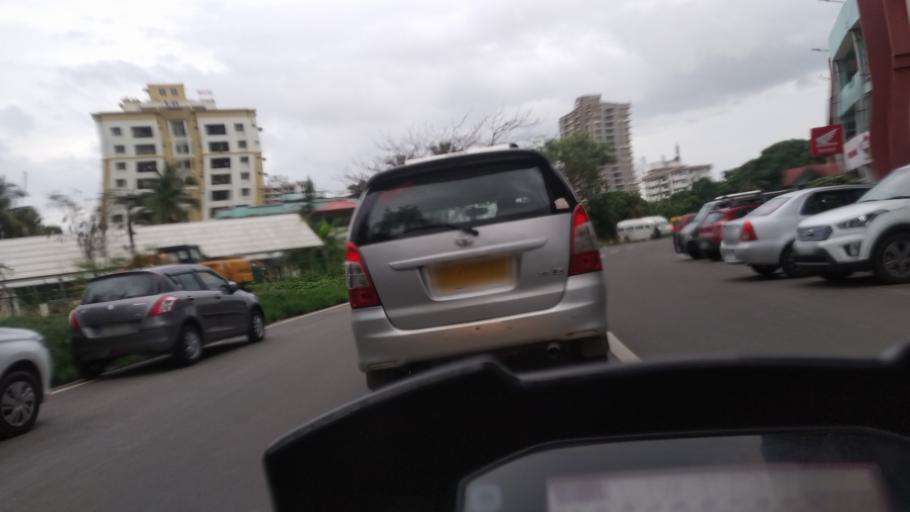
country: IN
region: Kerala
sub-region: Ernakulam
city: Cochin
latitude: 9.9969
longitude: 76.3020
